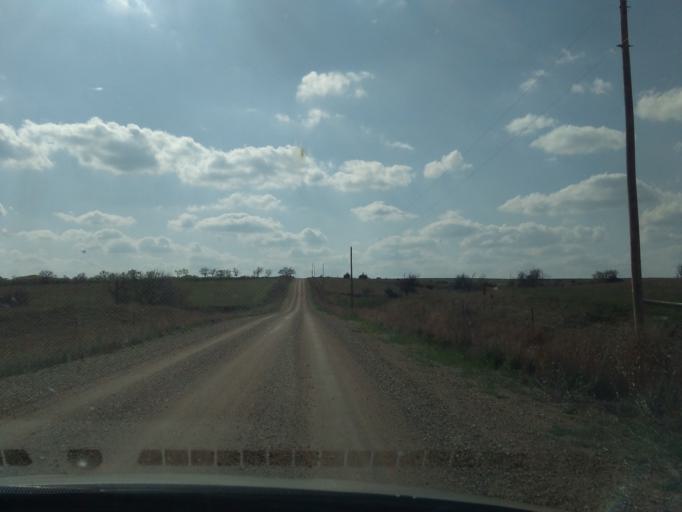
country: US
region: Nebraska
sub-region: Webster County
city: Red Cloud
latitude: 40.0314
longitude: -98.4387
